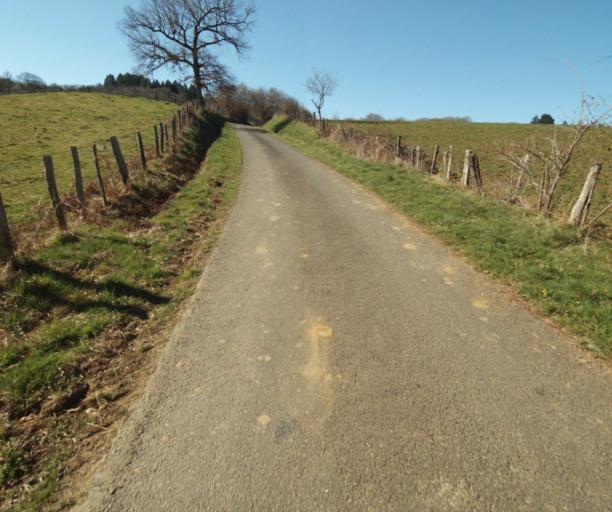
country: FR
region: Limousin
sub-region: Departement de la Correze
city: Chamboulive
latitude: 45.4179
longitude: 1.7051
